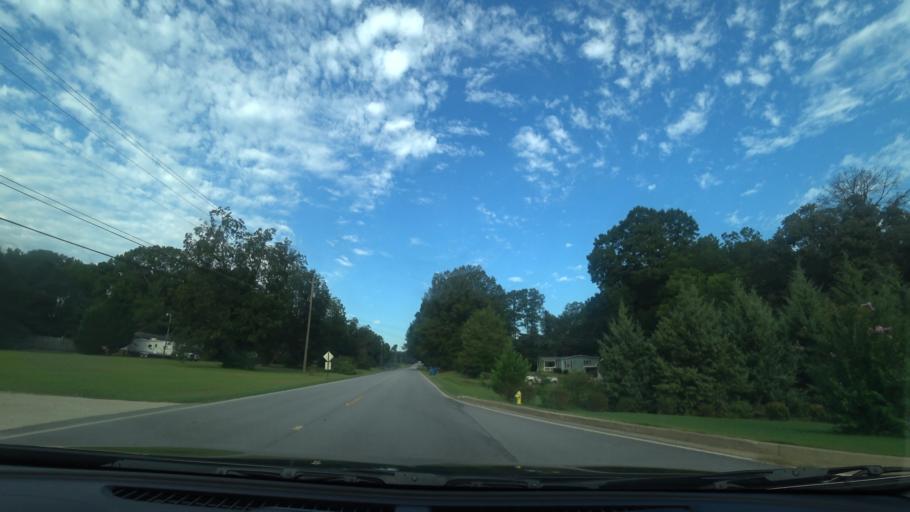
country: US
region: Georgia
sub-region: Newton County
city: Oakwood
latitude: 33.6123
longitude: -83.9524
